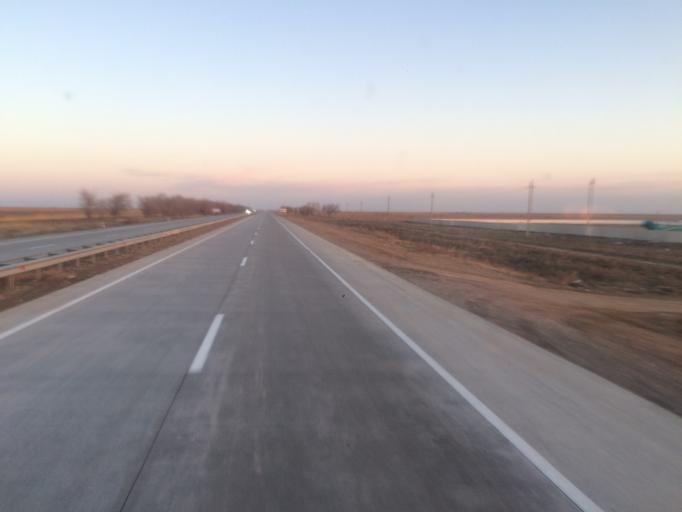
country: KZ
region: Ongtustik Qazaqstan
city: Bayaldyr
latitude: 43.0590
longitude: 68.6861
